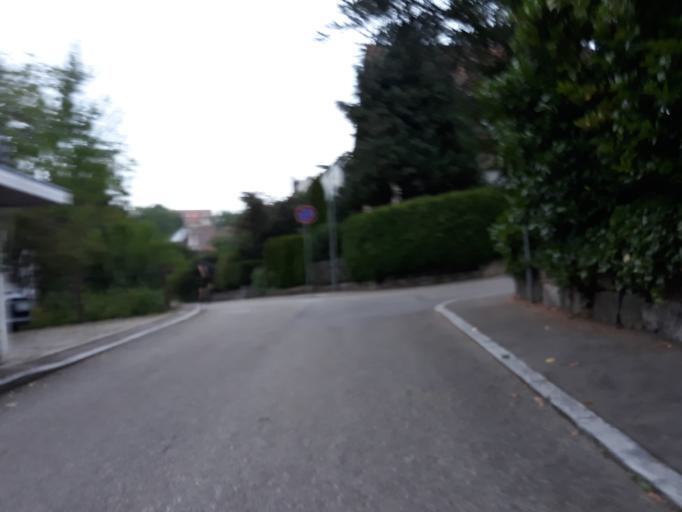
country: DE
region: Baden-Wuerttemberg
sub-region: Regierungsbezirk Stuttgart
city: Boeblingen
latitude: 48.6856
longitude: 9.0260
